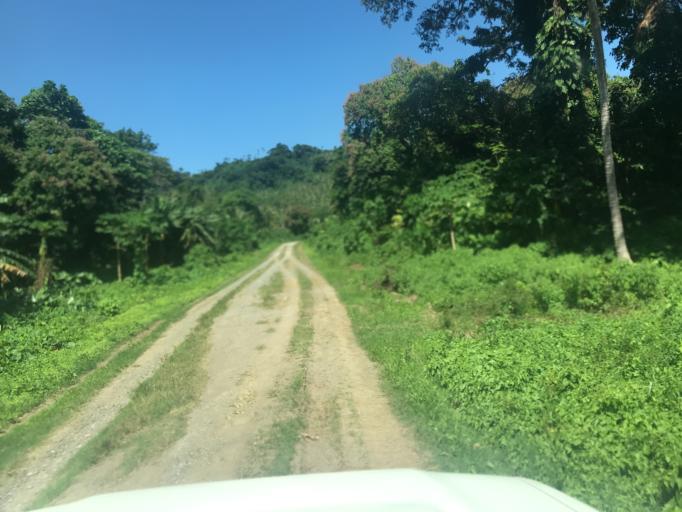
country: VU
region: Sanma
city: Luganville
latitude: -15.6048
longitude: 166.7826
